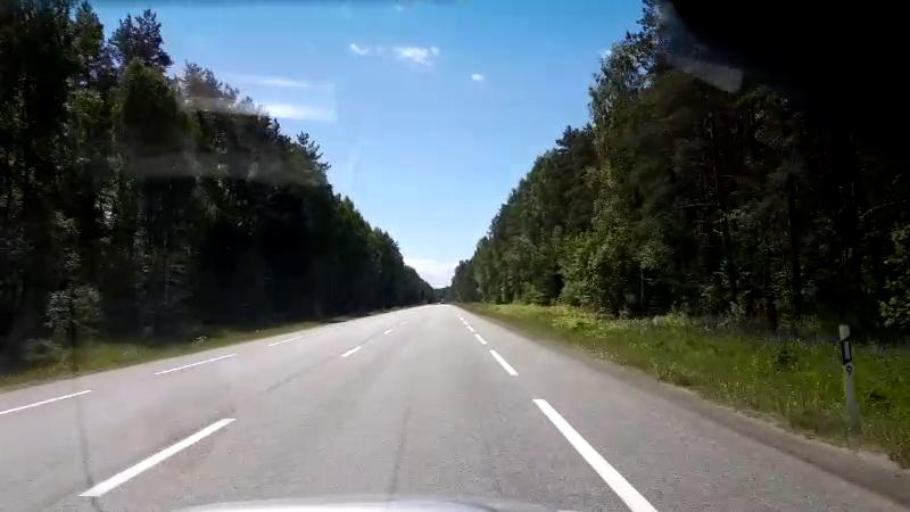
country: LV
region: Saulkrastu
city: Saulkrasti
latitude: 57.4606
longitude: 24.4329
